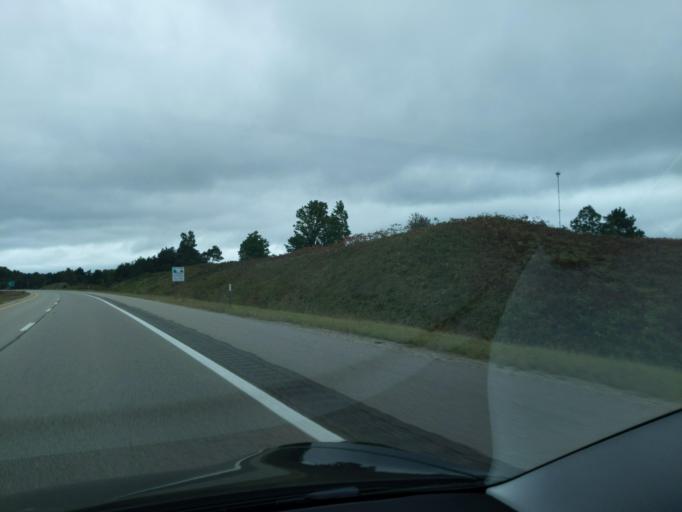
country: US
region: Michigan
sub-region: Wexford County
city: Manton
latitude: 44.3844
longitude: -85.3841
